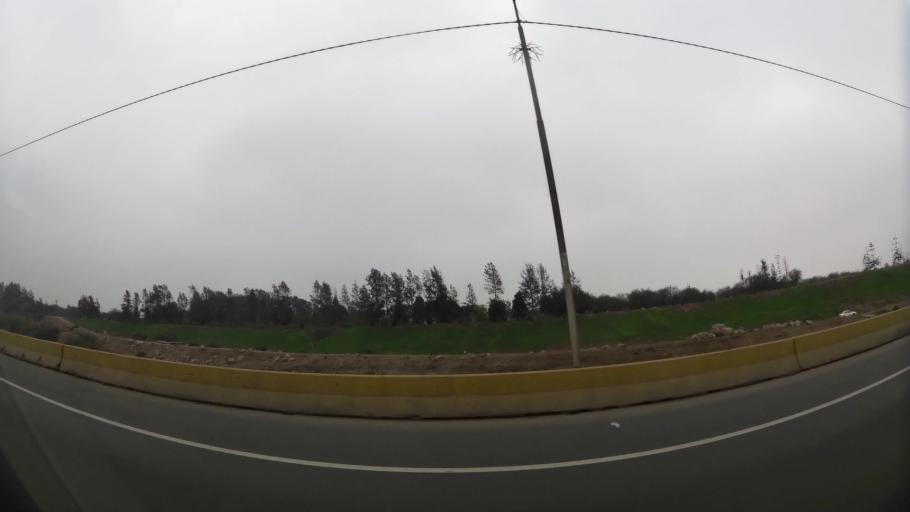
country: PE
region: Lima
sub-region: Lima
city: Vitarte
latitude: -12.0263
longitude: -76.9691
